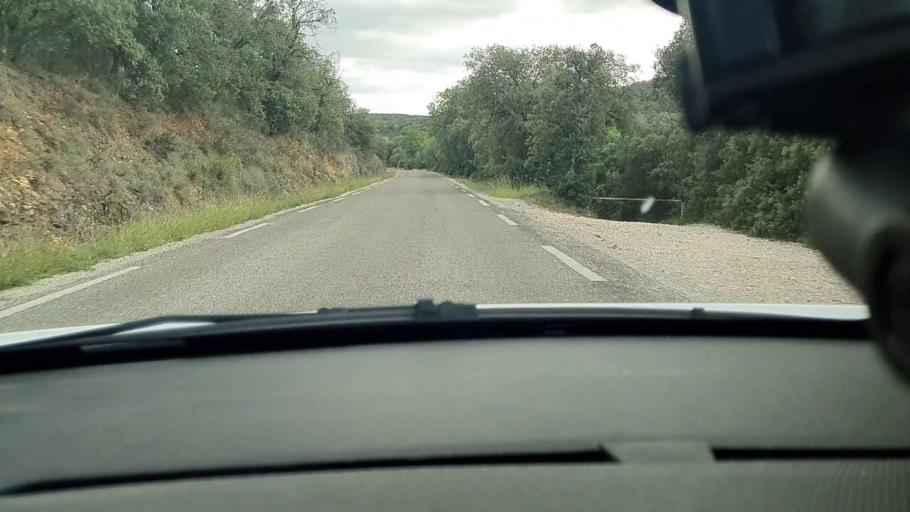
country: FR
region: Languedoc-Roussillon
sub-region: Departement du Gard
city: Les Mages
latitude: 44.2183
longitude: 4.1743
